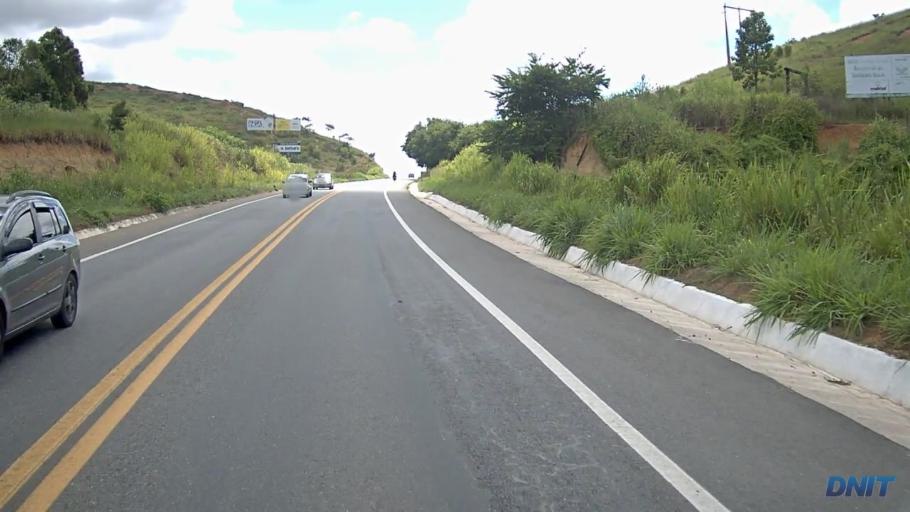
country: BR
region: Minas Gerais
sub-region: Governador Valadares
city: Governador Valadares
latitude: -18.9442
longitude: -42.0641
